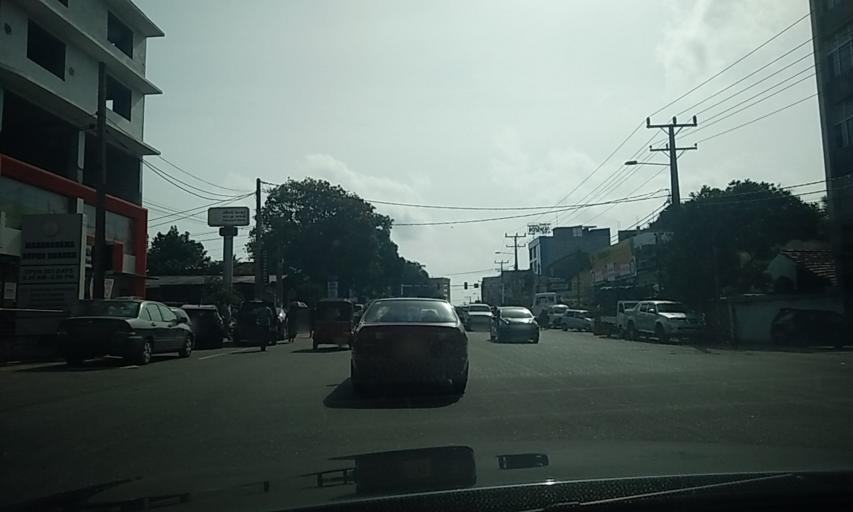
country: LK
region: Western
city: Maharagama
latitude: 6.8446
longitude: 79.9337
